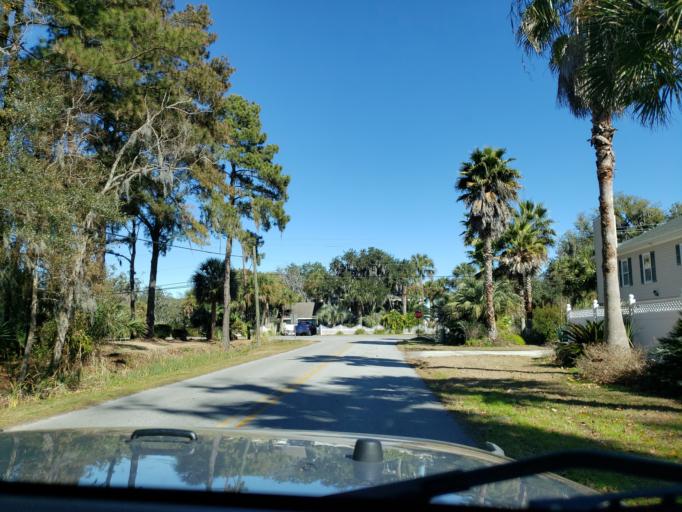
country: US
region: Georgia
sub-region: Chatham County
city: Whitemarsh Island
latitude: 32.0392
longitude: -80.9896
